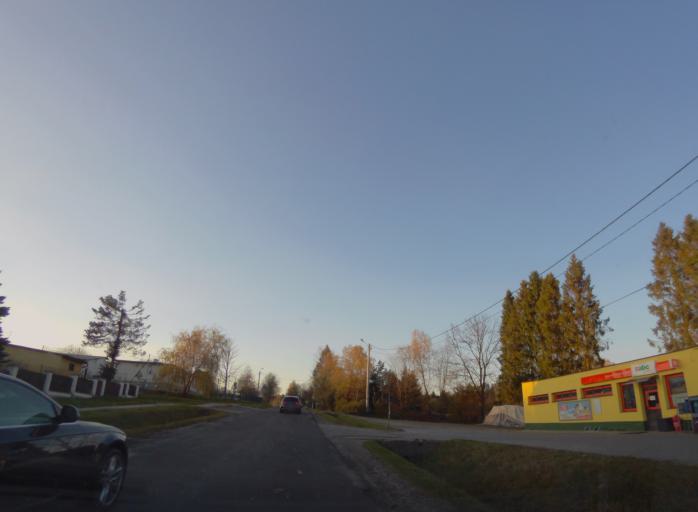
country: PL
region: Subcarpathian Voivodeship
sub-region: Powiat leski
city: Polanczyk
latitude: 49.3809
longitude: 22.4110
